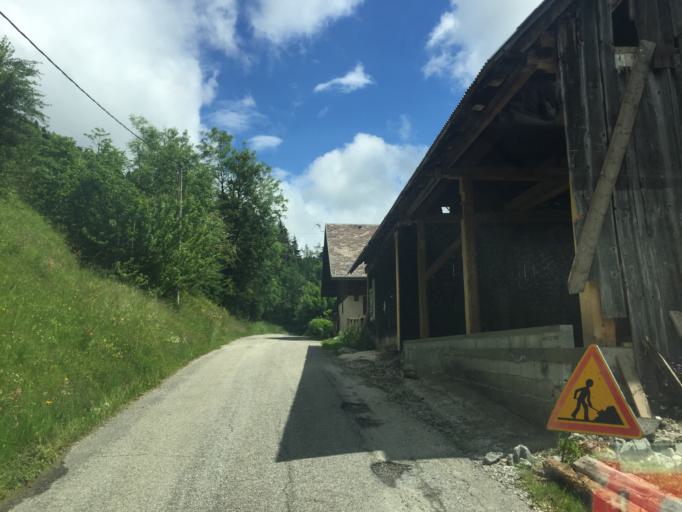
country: FR
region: Rhone-Alpes
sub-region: Departement de la Savoie
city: Cruet
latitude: 45.6154
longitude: 6.1113
